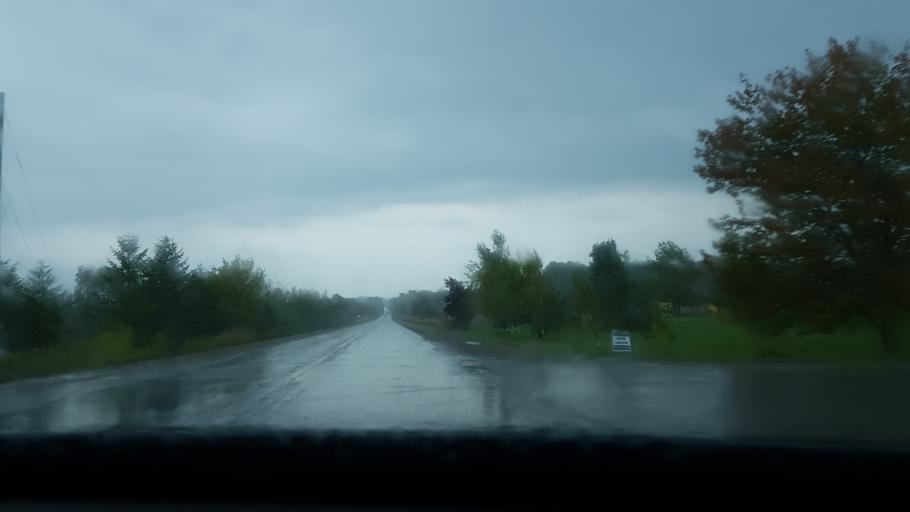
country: CA
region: Ontario
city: Omemee
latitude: 44.3821
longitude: -78.5517
